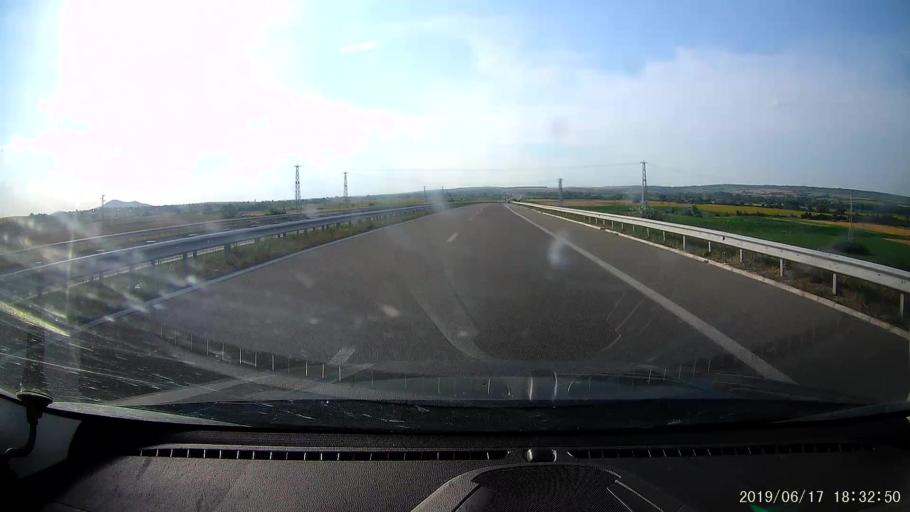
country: BG
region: Khaskovo
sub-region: Obshtina Dimitrovgrad
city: Dimitrovgrad
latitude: 42.0671
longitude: 25.4699
